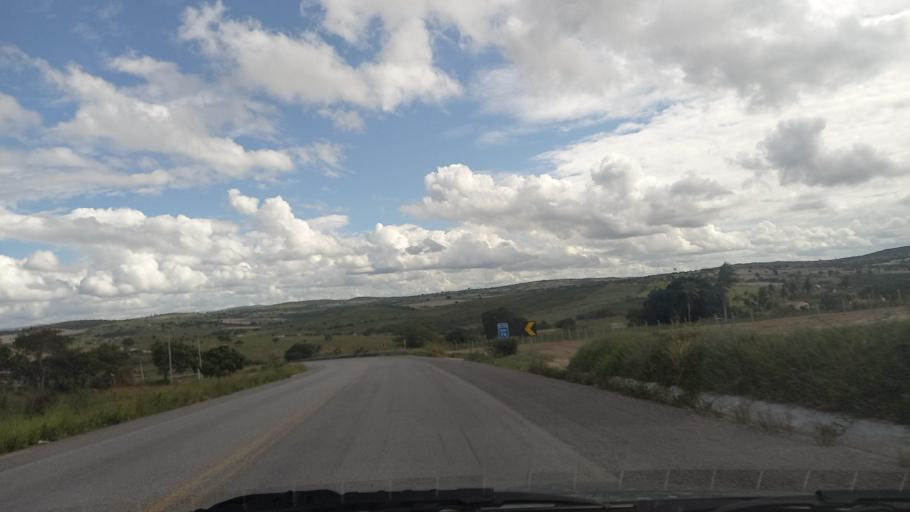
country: BR
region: Pernambuco
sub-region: Lajedo
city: Lajedo
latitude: -8.7263
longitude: -36.4308
